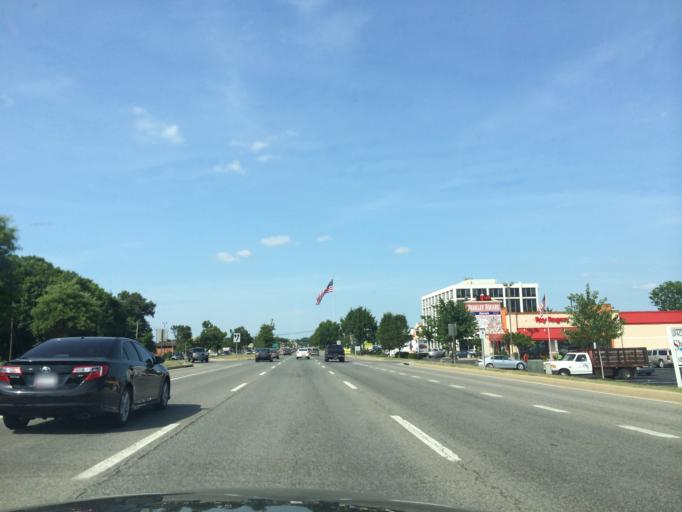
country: US
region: Maryland
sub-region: Charles County
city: Waldorf
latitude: 38.6359
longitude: -76.9006
